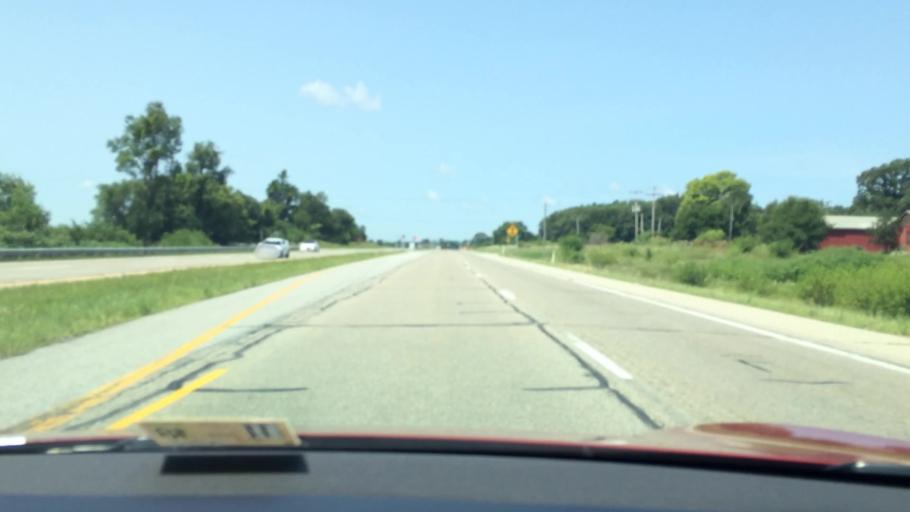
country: US
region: Indiana
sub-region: LaPorte County
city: Hudson Lake
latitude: 41.6729
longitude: -86.5812
